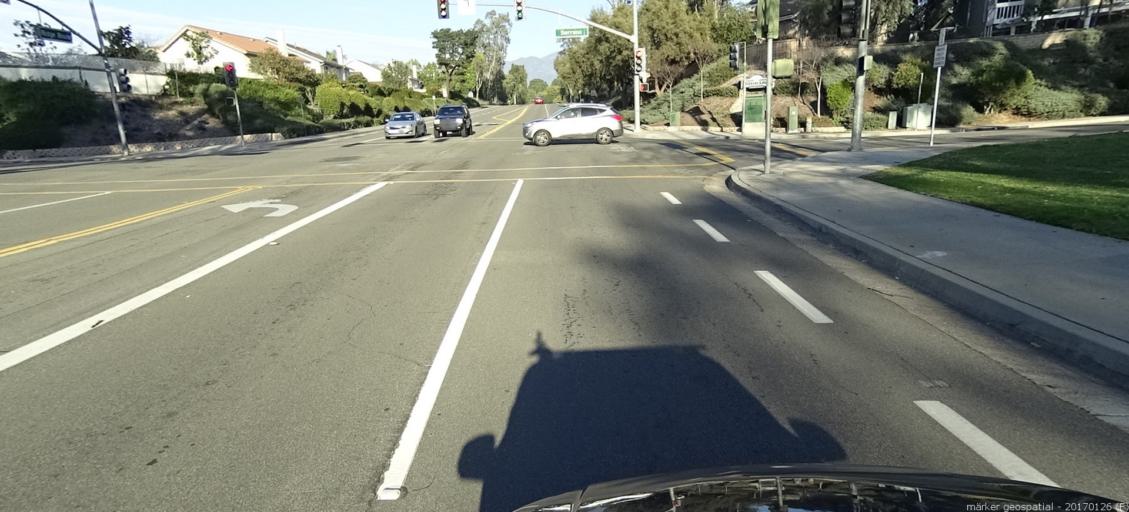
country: US
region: California
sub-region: Orange County
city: Lake Forest
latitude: 33.6395
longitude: -117.6881
